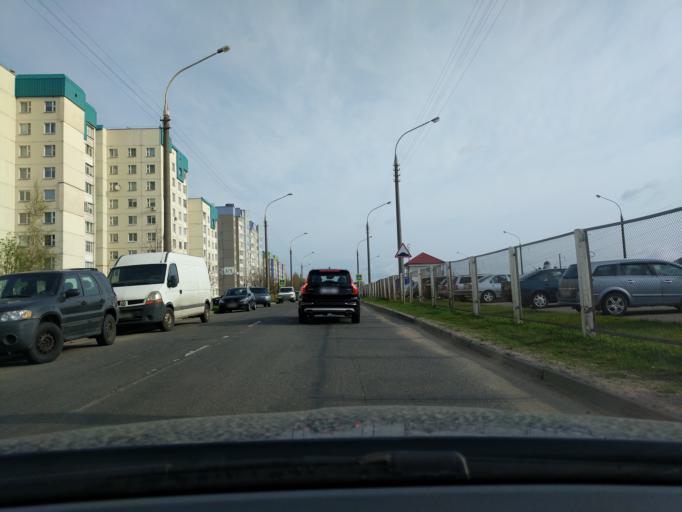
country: BY
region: Minsk
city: Novoye Medvezhino
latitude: 53.8970
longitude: 27.4632
